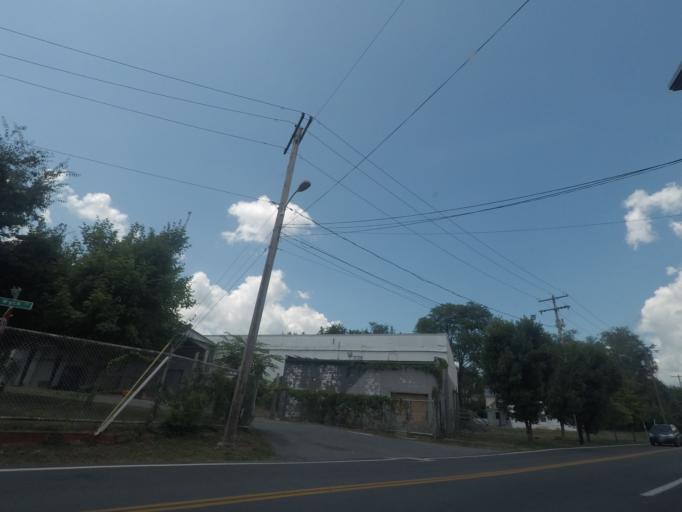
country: US
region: Virginia
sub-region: City of Winchester
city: Winchester
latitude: 39.1920
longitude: -78.1612
